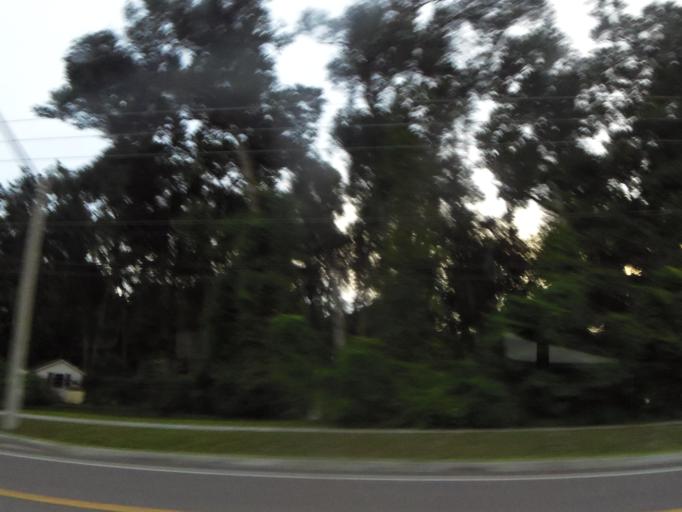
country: US
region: Florida
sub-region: Duval County
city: Jacksonville
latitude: 30.3643
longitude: -81.5559
